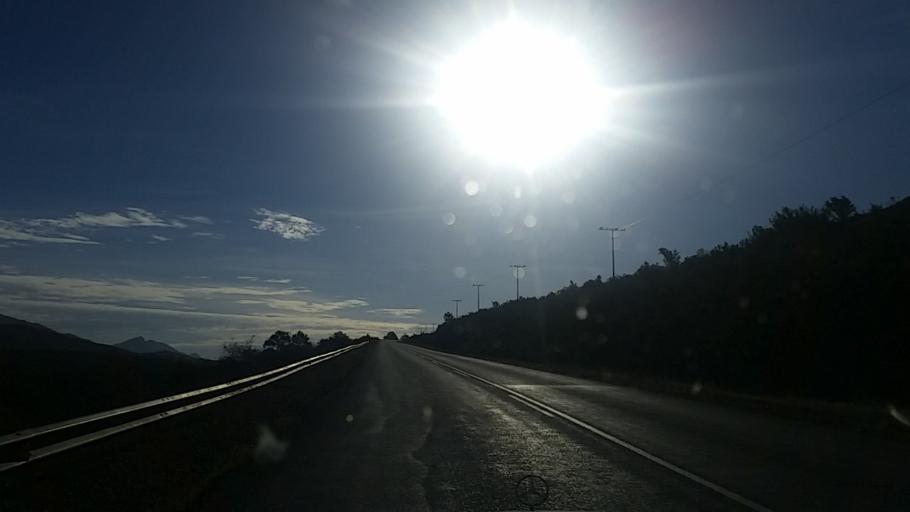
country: ZA
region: Western Cape
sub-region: Eden District Municipality
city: Knysna
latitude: -33.7600
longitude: 22.9595
